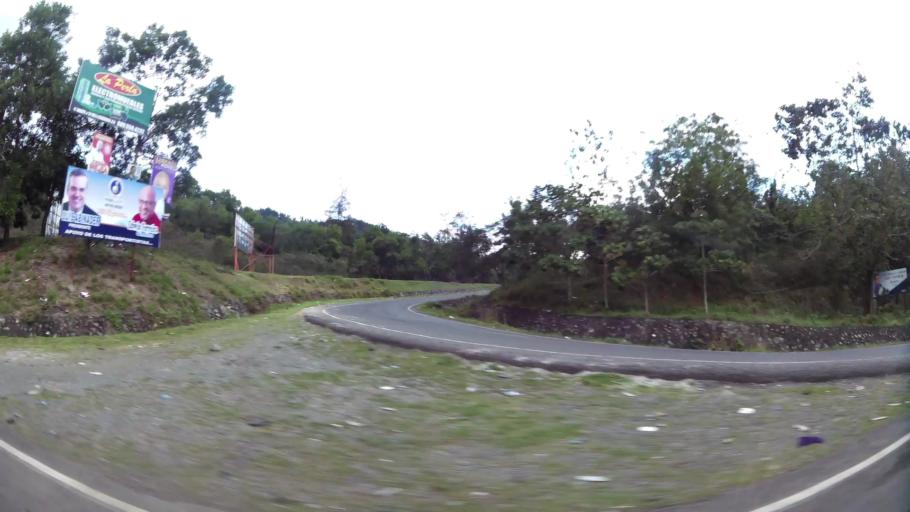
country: DO
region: San Cristobal
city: Villa Altagracia
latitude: 18.6922
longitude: -70.1848
